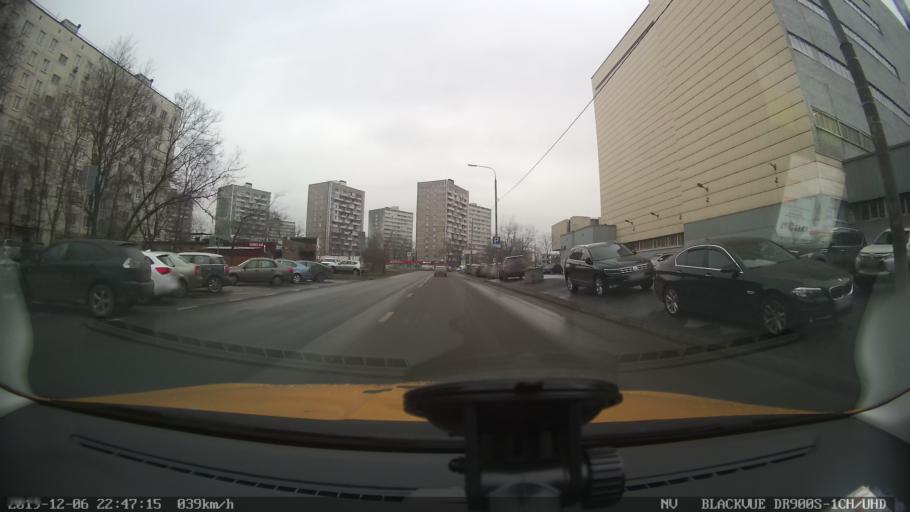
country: RU
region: Moscow
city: Metrogorodok
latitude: 55.8054
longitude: 37.7582
